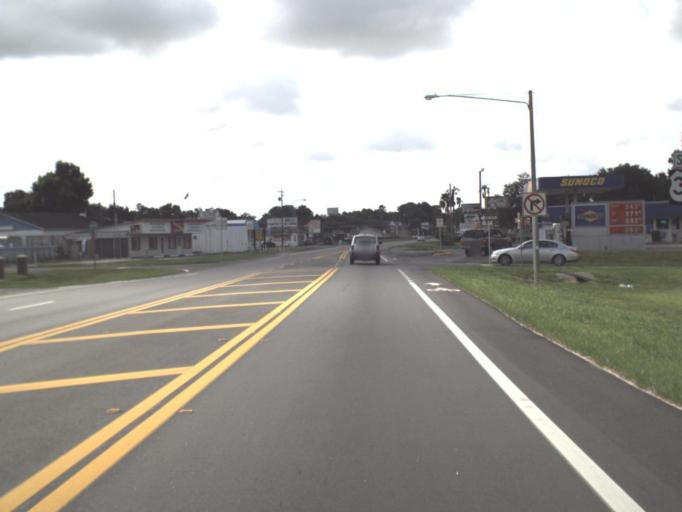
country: US
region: Florida
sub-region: Pasco County
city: Zephyrhills
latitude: 28.2435
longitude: -82.1881
